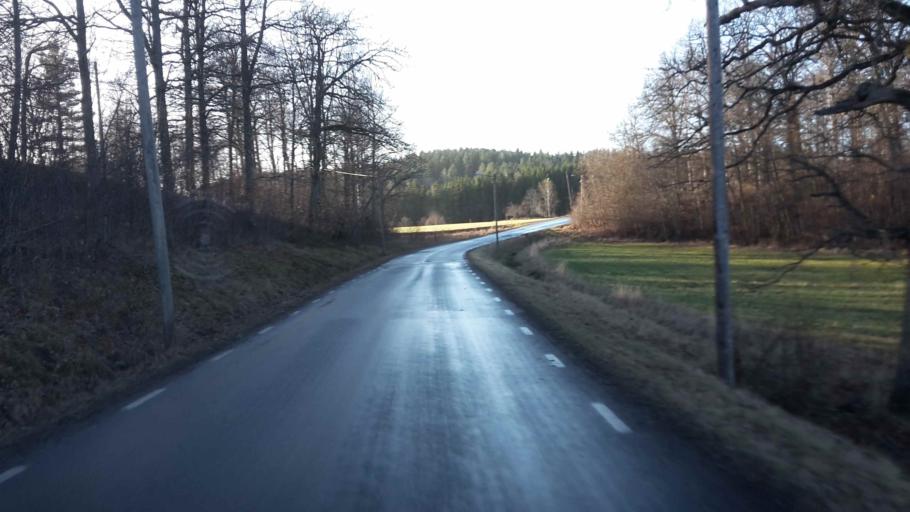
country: SE
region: Kalmar
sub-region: Vasterviks Kommun
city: Overum
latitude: 58.1496
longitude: 16.3235
